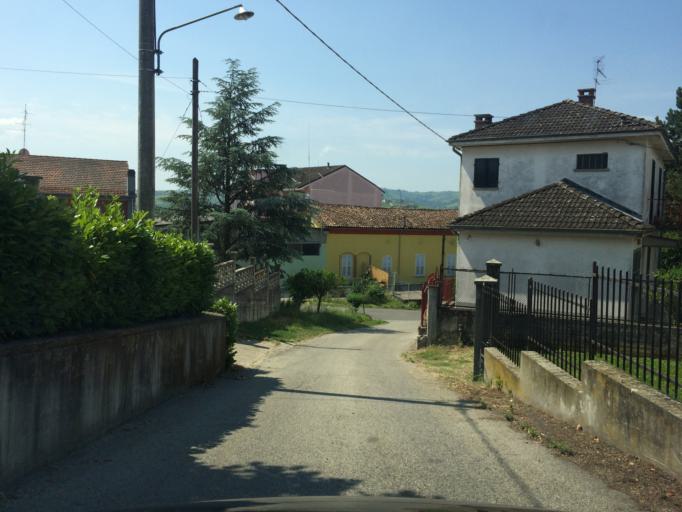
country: IT
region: Piedmont
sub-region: Provincia di Asti
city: Costigliole d'Asti
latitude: 44.7612
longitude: 8.2033
